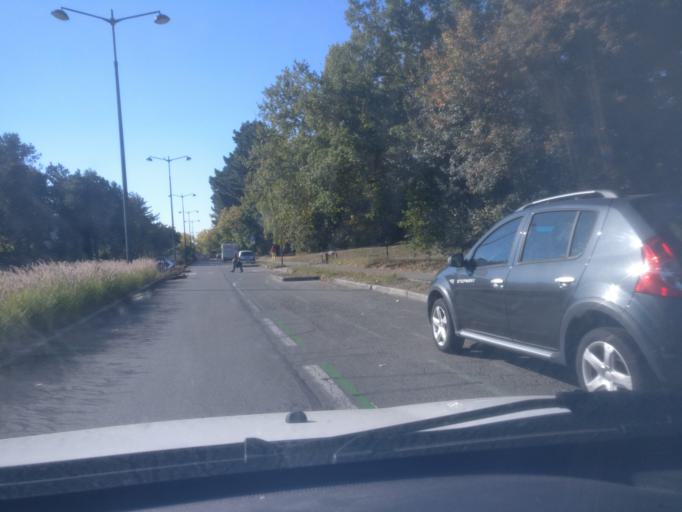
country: FR
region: Brittany
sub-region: Departement d'Ille-et-Vilaine
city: Rennes
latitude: 48.1366
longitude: -1.6646
